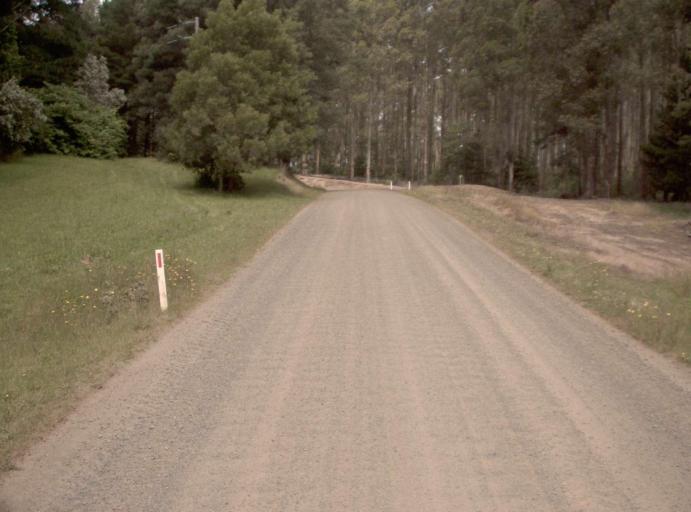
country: AU
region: Victoria
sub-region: Latrobe
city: Traralgon
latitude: -38.3736
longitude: 146.6845
